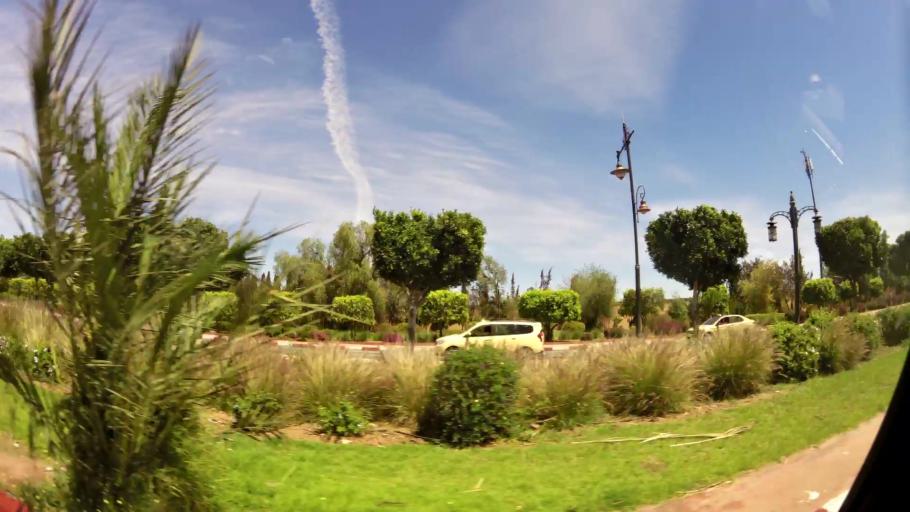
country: MA
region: Marrakech-Tensift-Al Haouz
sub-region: Marrakech
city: Marrakesh
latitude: 31.6157
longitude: -7.9961
